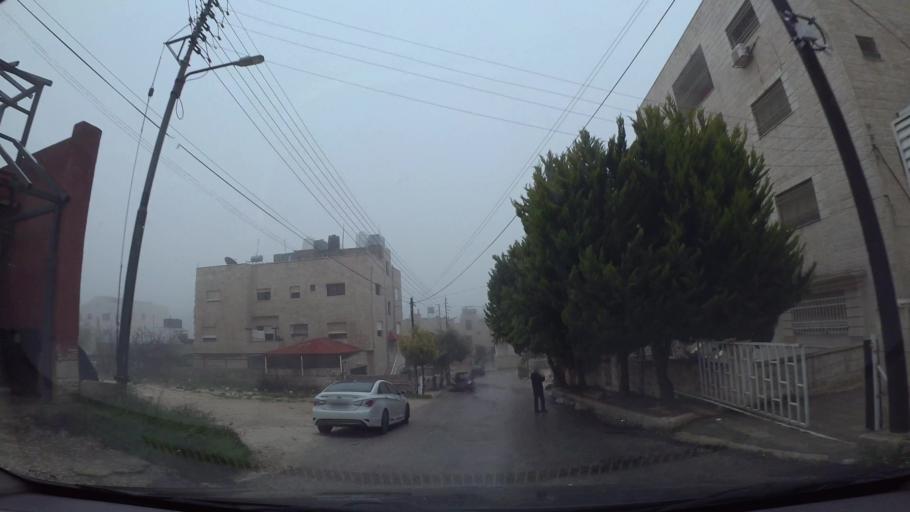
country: JO
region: Amman
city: Al Jubayhah
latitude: 32.0197
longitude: 35.8797
